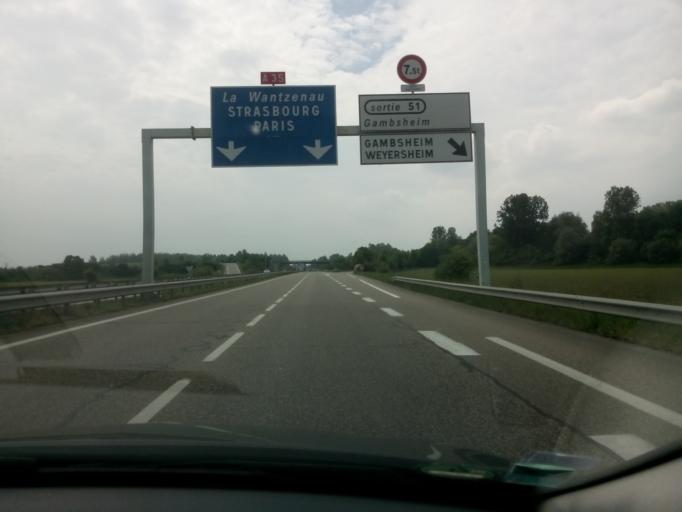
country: FR
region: Alsace
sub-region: Departement du Bas-Rhin
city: Gambsheim
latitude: 48.7088
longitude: 7.8591
